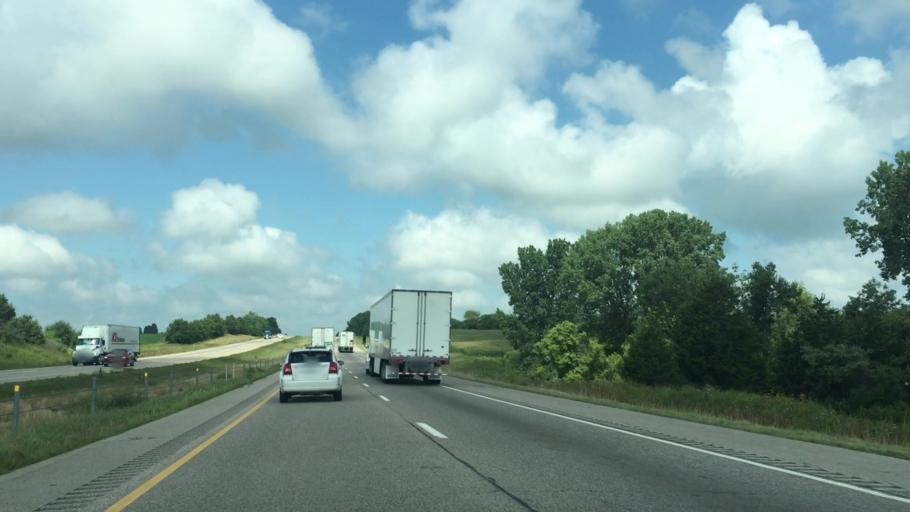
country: US
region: Iowa
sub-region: Muscatine County
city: West Liberty
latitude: 41.6540
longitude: -91.1853
